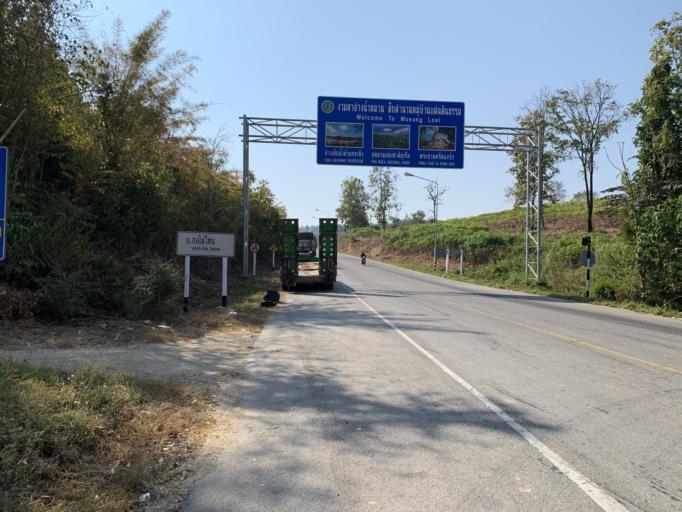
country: TH
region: Loei
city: Tha Li
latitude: 17.5782
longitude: 101.5474
